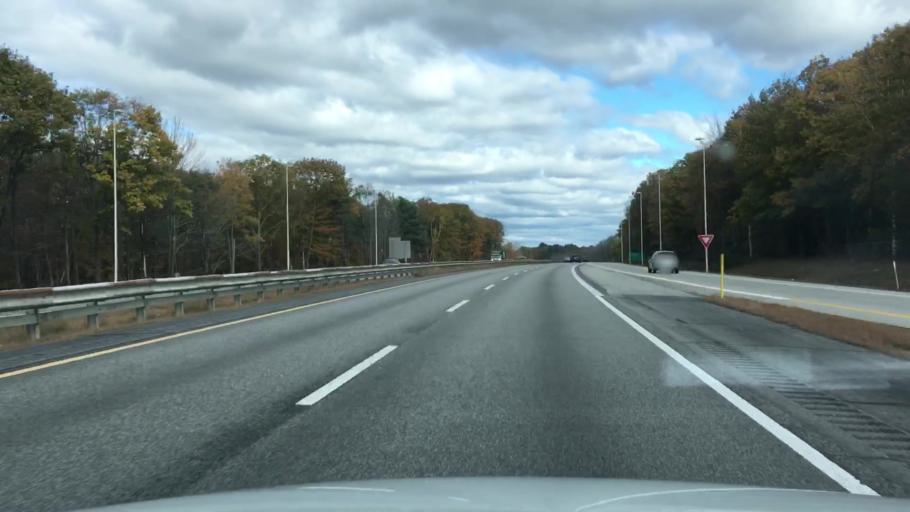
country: US
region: Maine
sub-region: Cumberland County
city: Freeport
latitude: 43.8460
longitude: -70.1191
